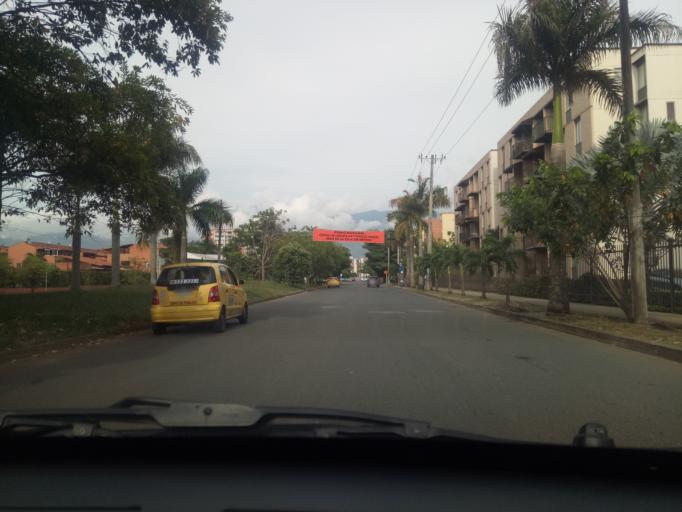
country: CO
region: Valle del Cauca
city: Cali
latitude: 3.3684
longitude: -76.5181
